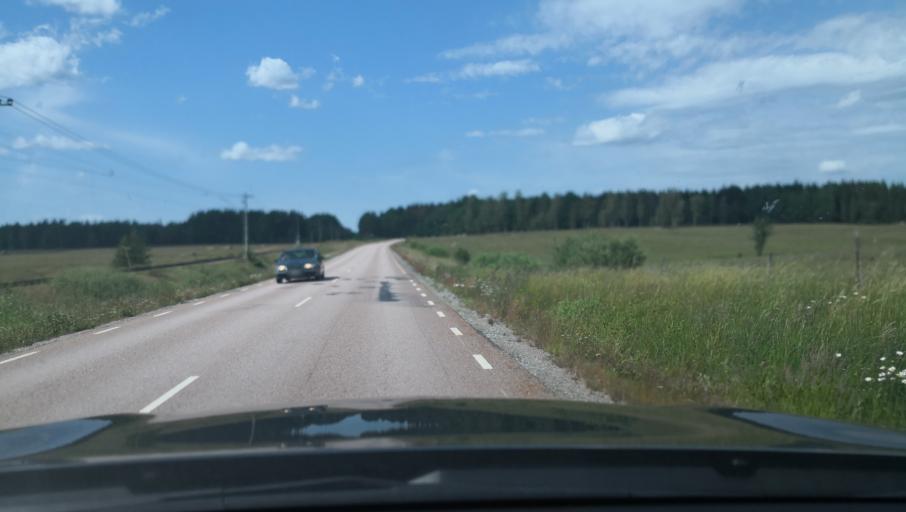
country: SE
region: Vaestmanland
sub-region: Surahammars Kommun
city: Ramnas
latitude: 59.8396
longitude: 16.1224
